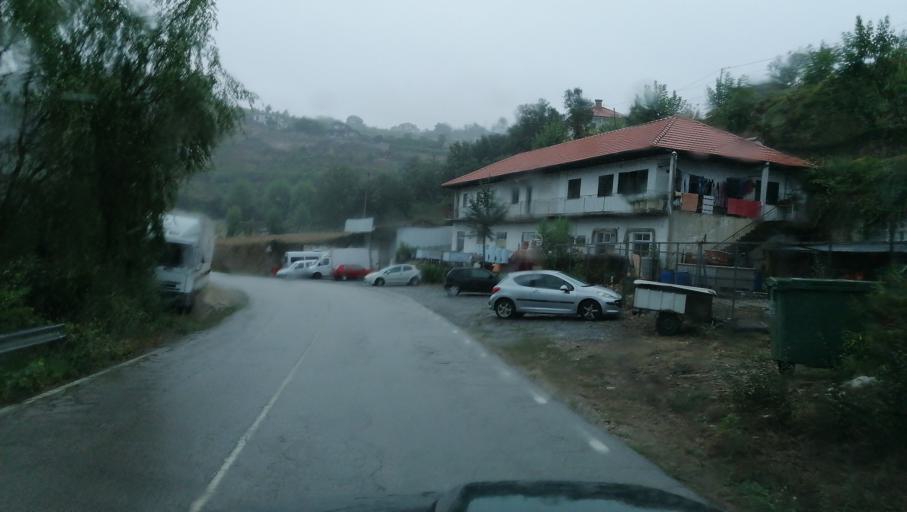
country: PT
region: Braga
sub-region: Cabeceiras de Basto
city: Cabeceiras de Basto
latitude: 41.4894
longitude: -7.9571
